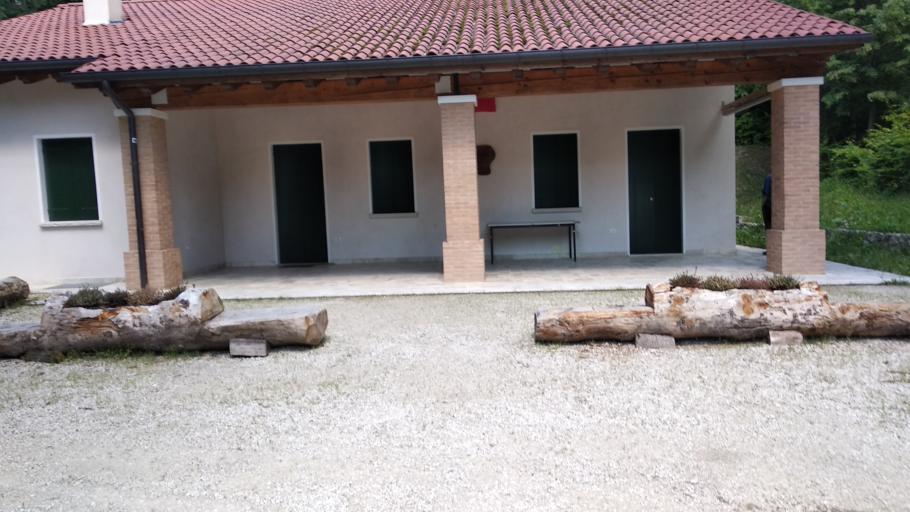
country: IT
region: Veneto
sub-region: Provincia di Treviso
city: Crespano del Grappa
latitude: 45.8482
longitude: 11.8392
